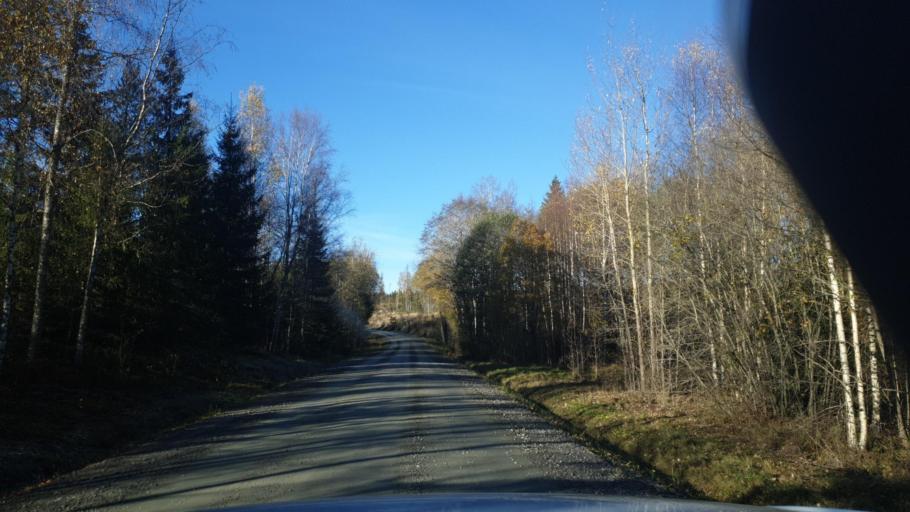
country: SE
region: Vaermland
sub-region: Karlstads Kommun
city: Edsvalla
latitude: 59.4425
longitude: 13.1814
